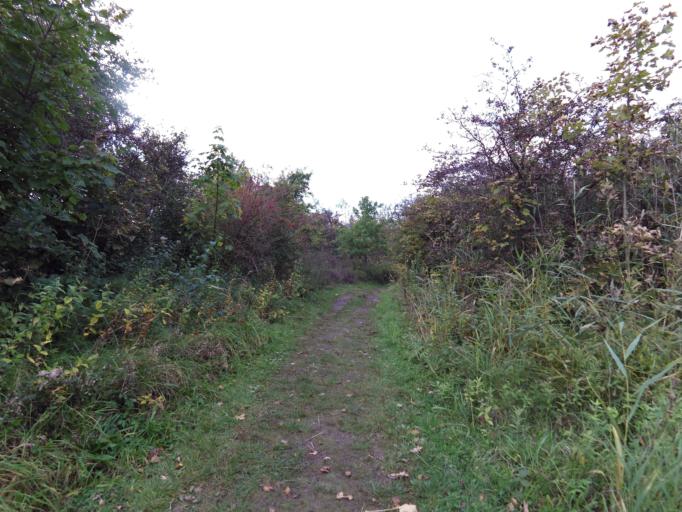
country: NL
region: South Holland
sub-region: Gemeente Hellevoetsluis
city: Nieuw-Helvoet
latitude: 51.8492
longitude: 4.0727
